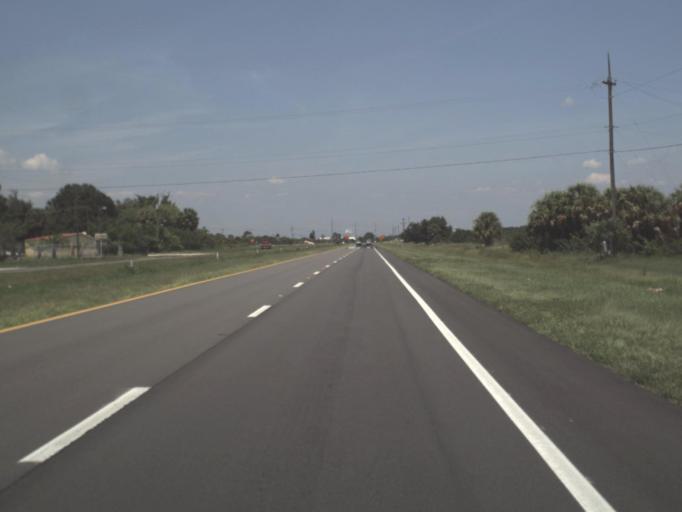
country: US
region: Florida
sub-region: Hillsborough County
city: Ruskin
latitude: 27.6782
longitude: -82.4773
